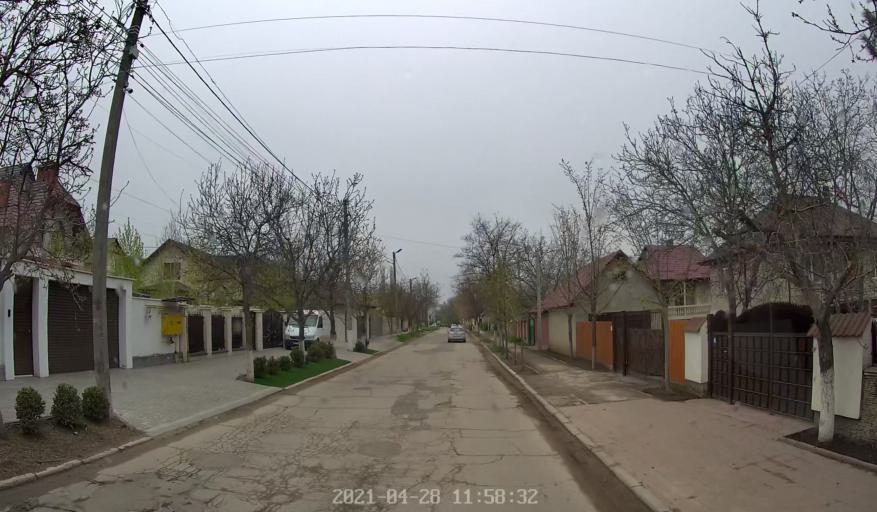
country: MD
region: Chisinau
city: Singera
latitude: 46.9795
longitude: 28.9338
